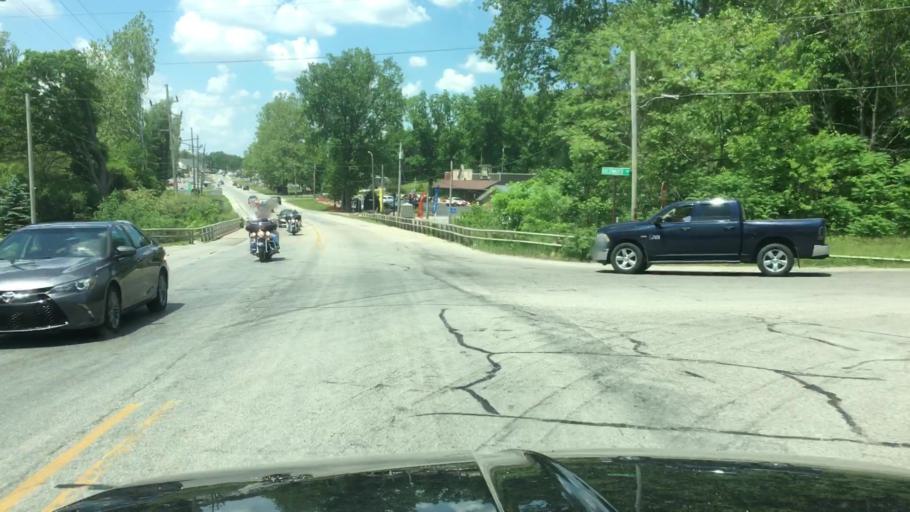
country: US
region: Indiana
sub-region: Kosciusko County
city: North Webster
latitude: 41.3160
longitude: -85.6920
